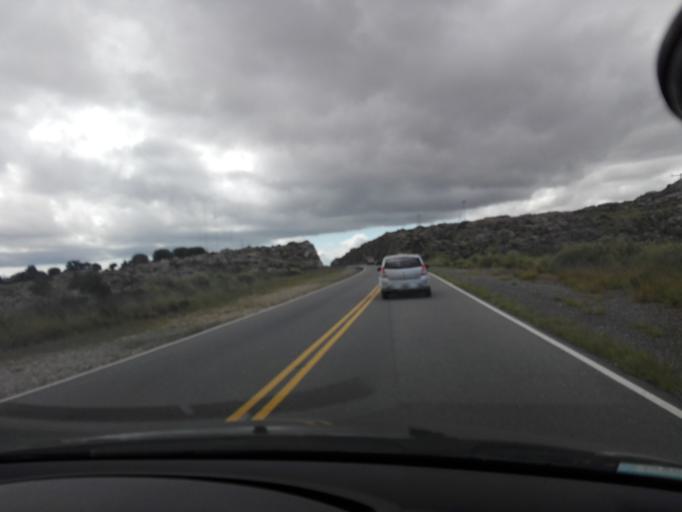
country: AR
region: Cordoba
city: Villa Cura Brochero
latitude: -31.6151
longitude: -64.8992
